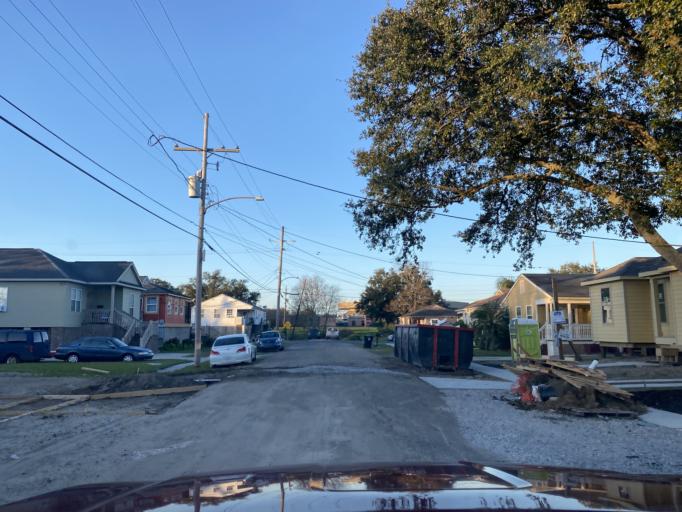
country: US
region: Louisiana
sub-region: Orleans Parish
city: New Orleans
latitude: 30.0253
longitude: -90.0510
